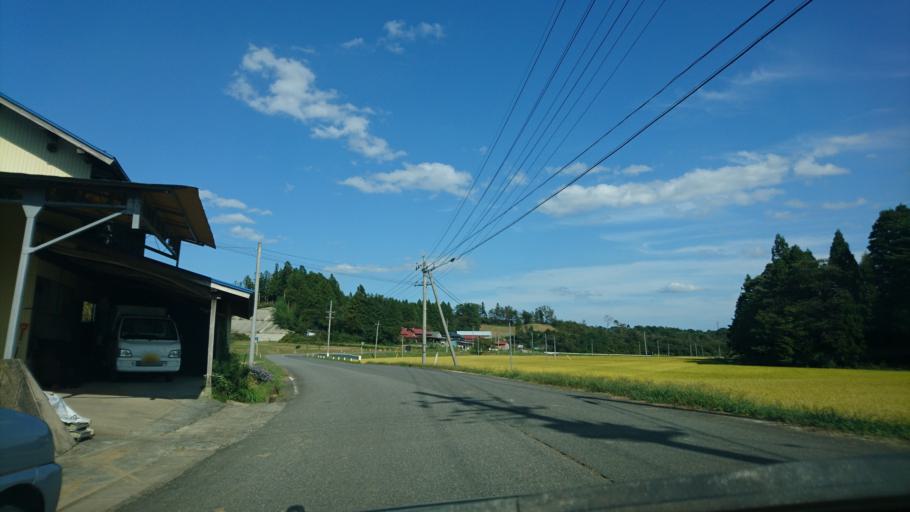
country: JP
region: Iwate
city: Ichinoseki
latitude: 38.8790
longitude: 141.0608
